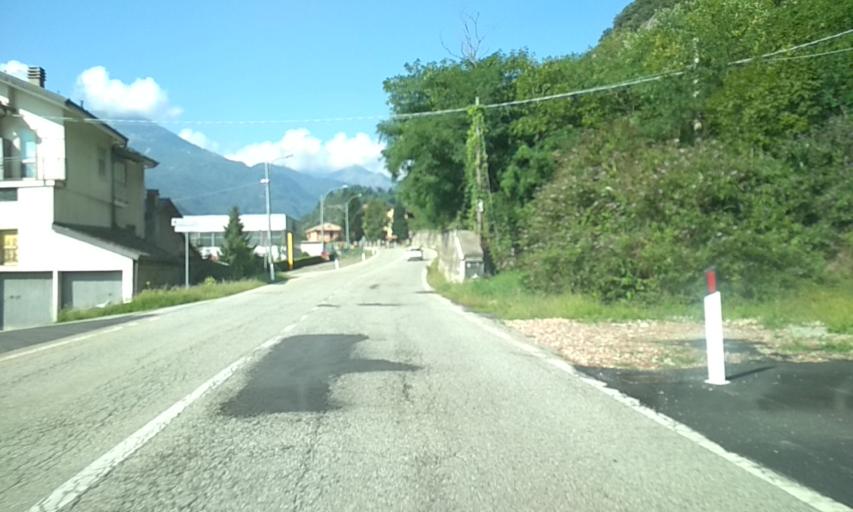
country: IT
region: Piedmont
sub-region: Provincia di Torino
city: Alpette
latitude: 45.4194
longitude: 7.5635
